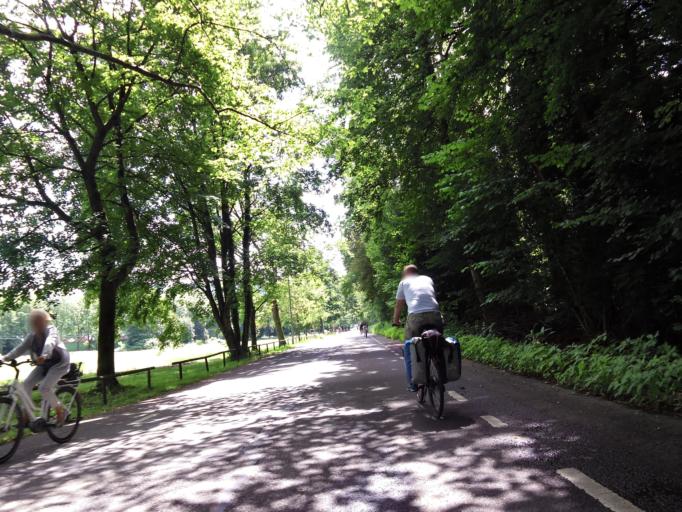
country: AT
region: Vorarlberg
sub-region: Politischer Bezirk Bregenz
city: Horbranz
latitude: 47.5442
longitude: 9.7244
